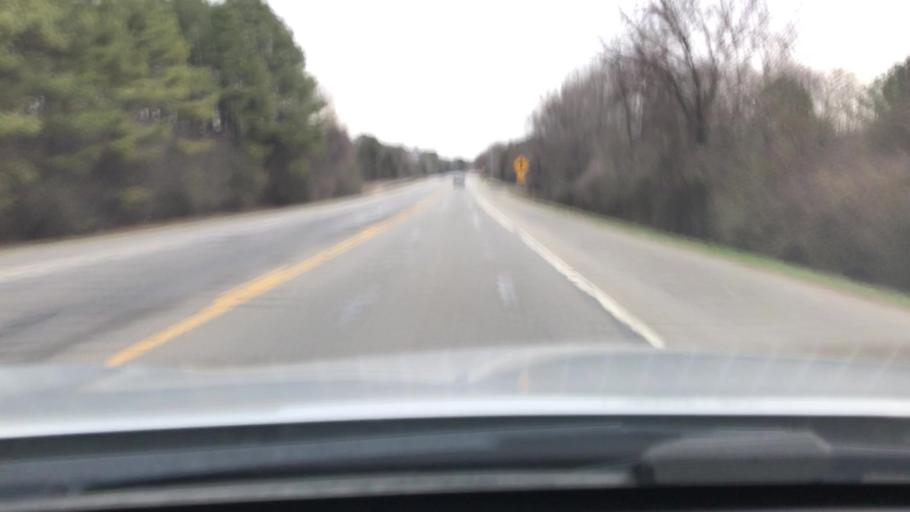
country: US
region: Arkansas
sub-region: Hempstead County
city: Hope
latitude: 33.6879
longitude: -93.5879
